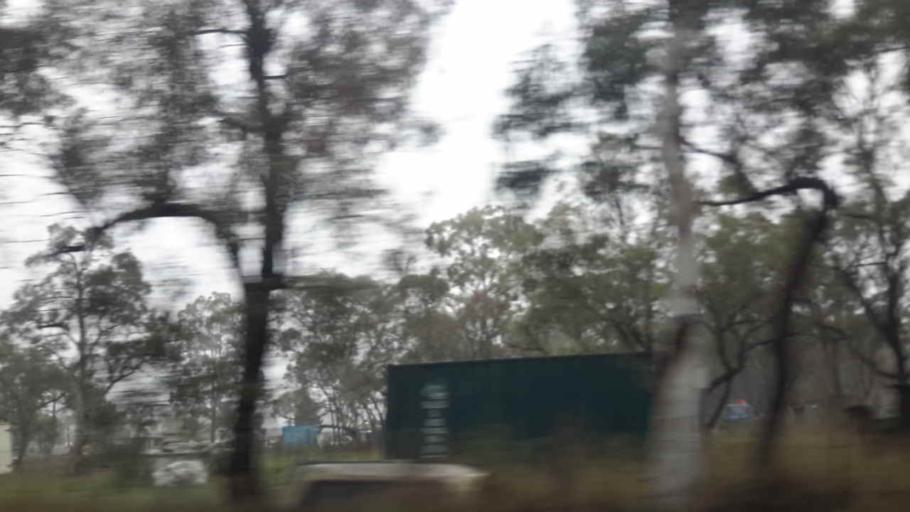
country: AU
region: New South Wales
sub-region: Hawkesbury
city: South Windsor
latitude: -33.6524
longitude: 150.7741
